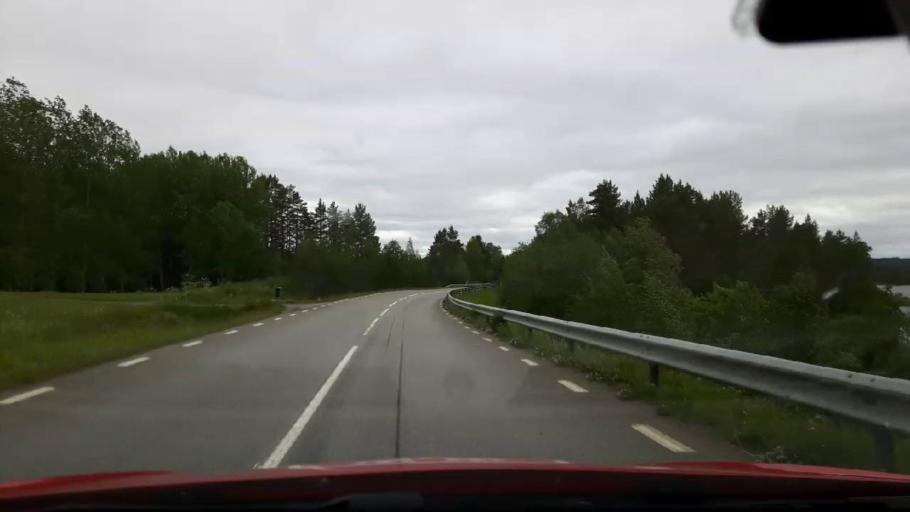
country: SE
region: Jaemtland
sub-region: Stroemsunds Kommun
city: Stroemsund
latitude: 63.4915
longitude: 15.4520
